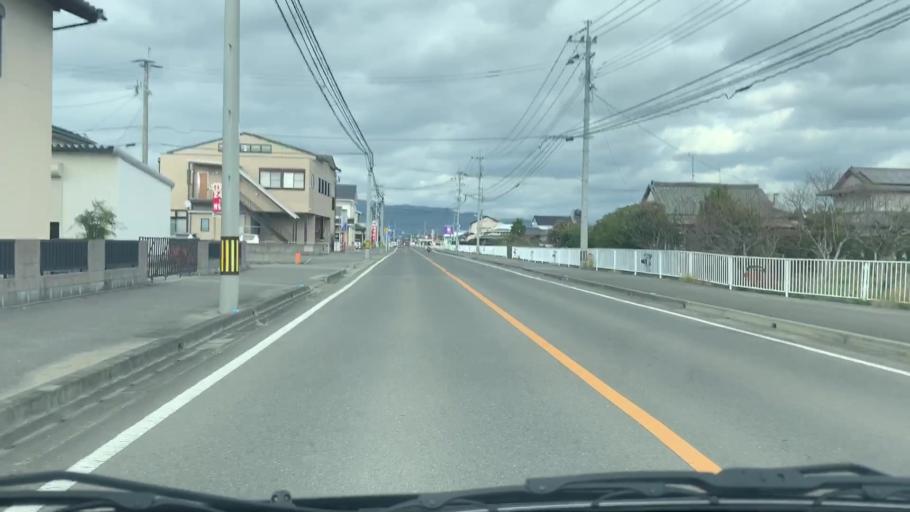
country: JP
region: Saga Prefecture
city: Saga-shi
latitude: 33.2458
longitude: 130.2379
